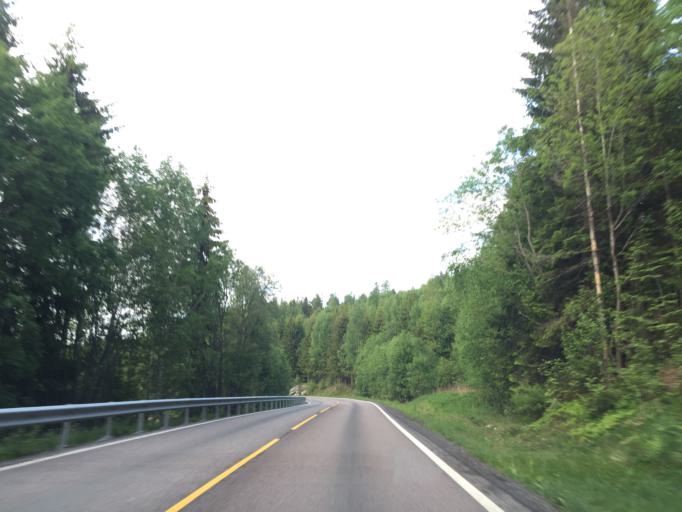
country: NO
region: Akershus
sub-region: Fet
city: Fetsund
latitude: 59.9499
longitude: 11.2010
